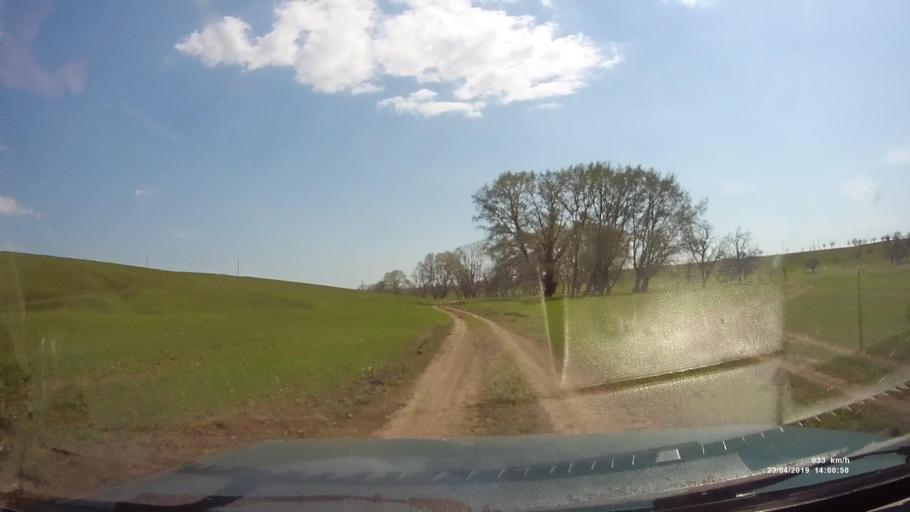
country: RU
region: Rostov
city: Remontnoye
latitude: 46.5577
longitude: 42.9473
